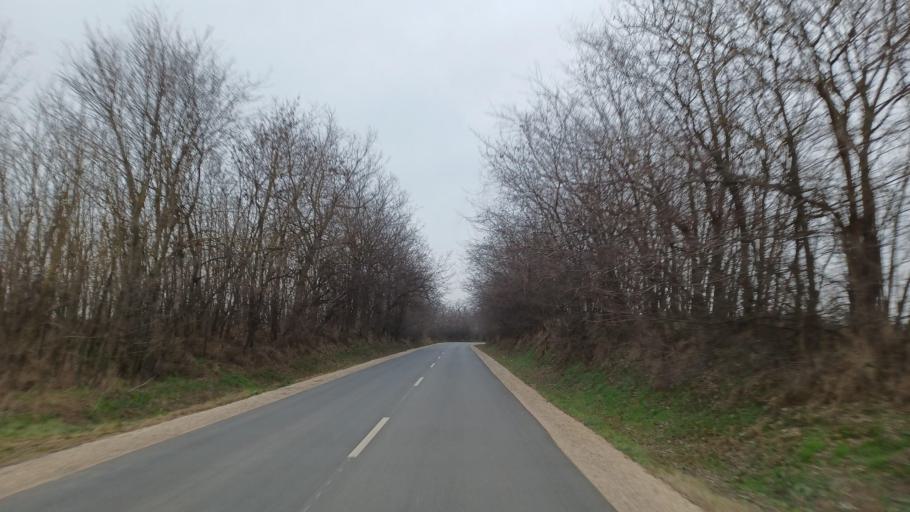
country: HU
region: Tolna
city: Nagydorog
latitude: 46.5749
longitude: 18.6349
